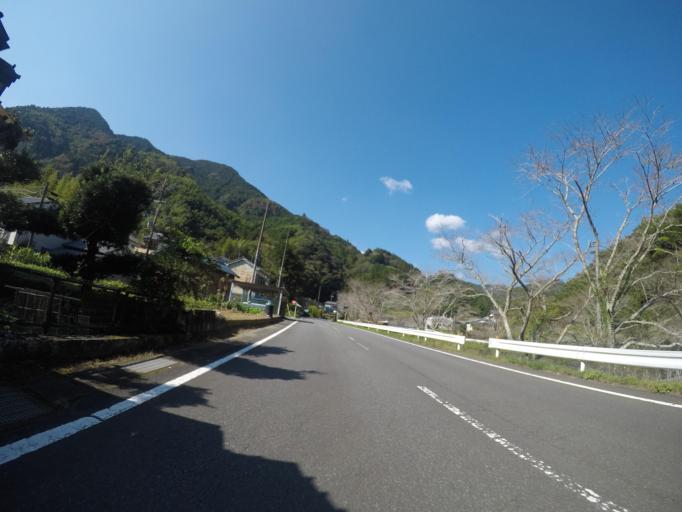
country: JP
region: Shizuoka
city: Fujinomiya
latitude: 35.1385
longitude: 138.4717
